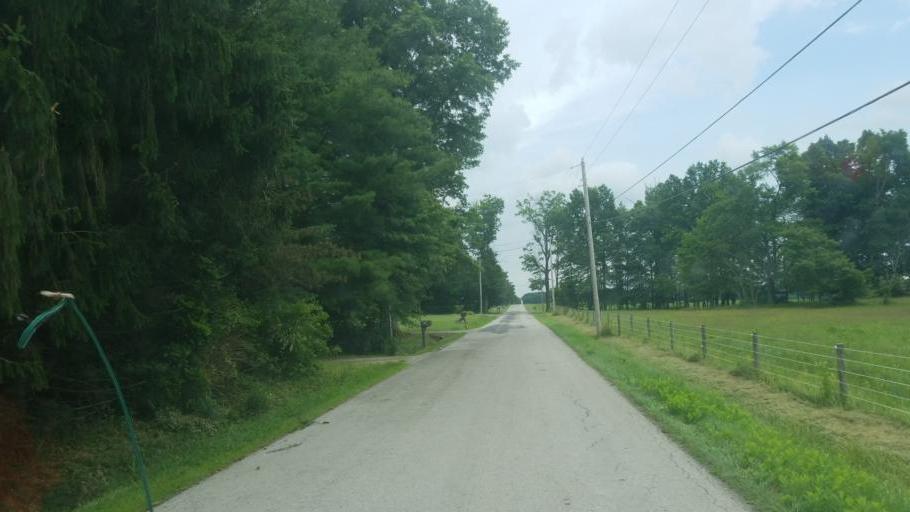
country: US
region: Ohio
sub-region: Wayne County
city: Wooster
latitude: 40.8945
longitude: -81.9458
